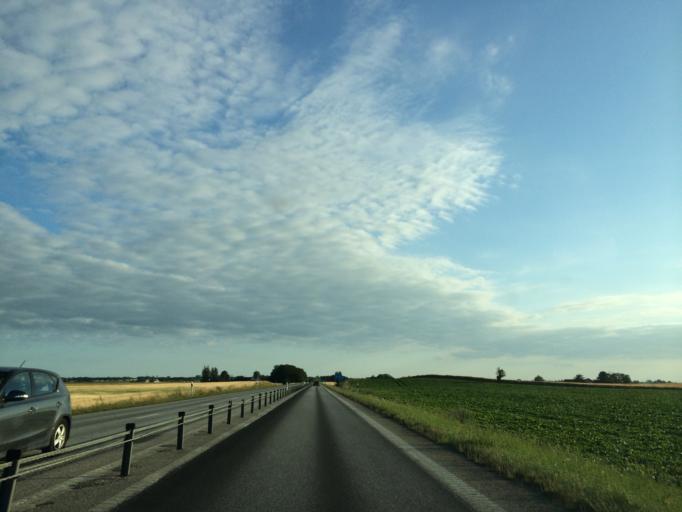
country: SE
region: Skane
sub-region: Vellinge Kommun
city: Vellinge
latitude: 55.4455
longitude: 12.9948
